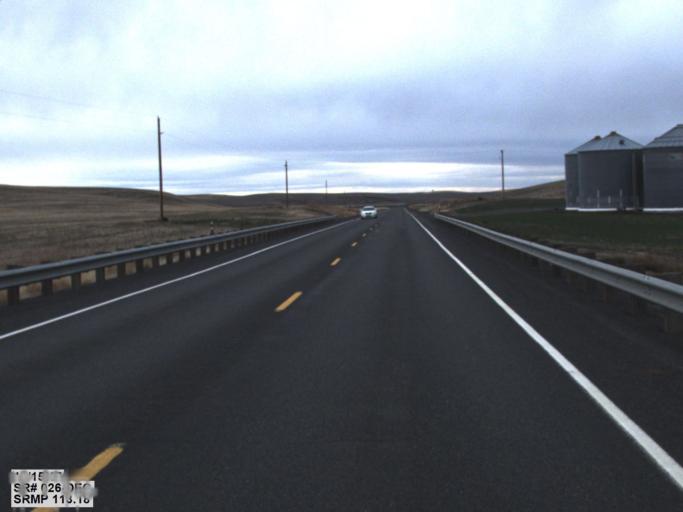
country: US
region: Washington
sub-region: Garfield County
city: Pomeroy
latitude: 46.8076
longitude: -117.7295
